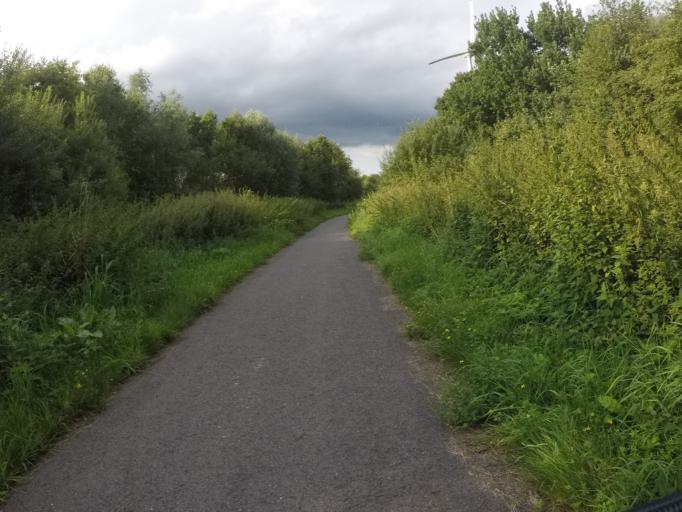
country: DE
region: North Rhine-Westphalia
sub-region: Regierungsbezirk Munster
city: Isselburg
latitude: 51.8165
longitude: 6.5317
